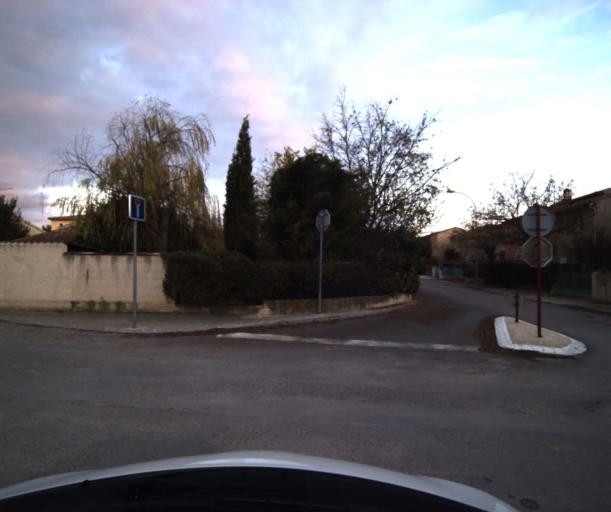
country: FR
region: Provence-Alpes-Cote d'Azur
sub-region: Departement du Vaucluse
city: Pertuis
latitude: 43.6976
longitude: 5.4856
